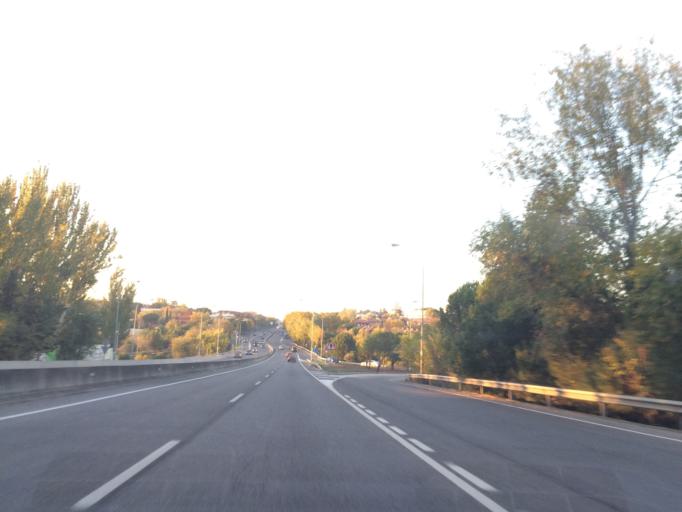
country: ES
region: Madrid
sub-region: Provincia de Madrid
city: Moncloa-Aravaca
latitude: 40.4522
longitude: -3.7645
